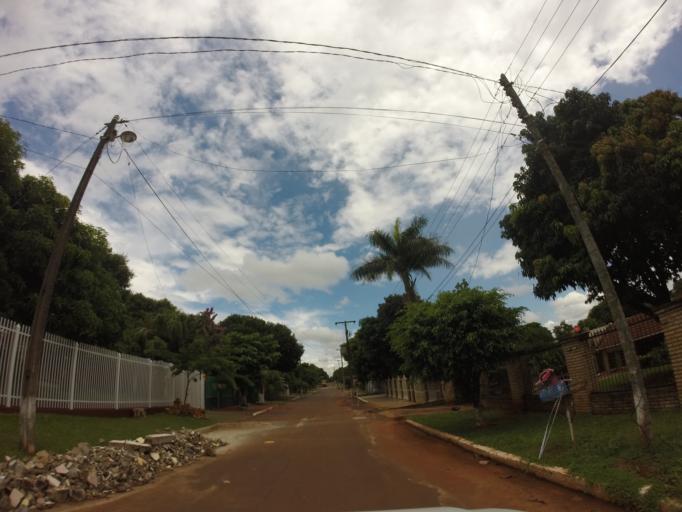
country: PY
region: Alto Parana
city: Ciudad del Este
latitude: -25.4155
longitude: -54.6312
